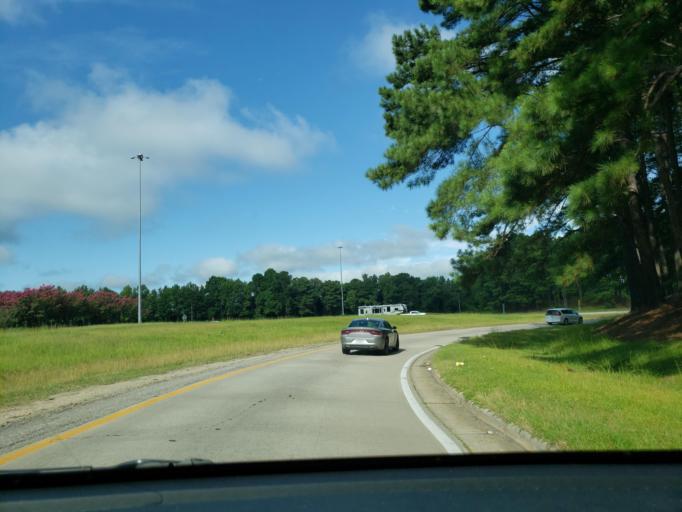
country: US
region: North Carolina
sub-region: Nash County
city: Red Oak
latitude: 35.9802
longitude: -77.8758
